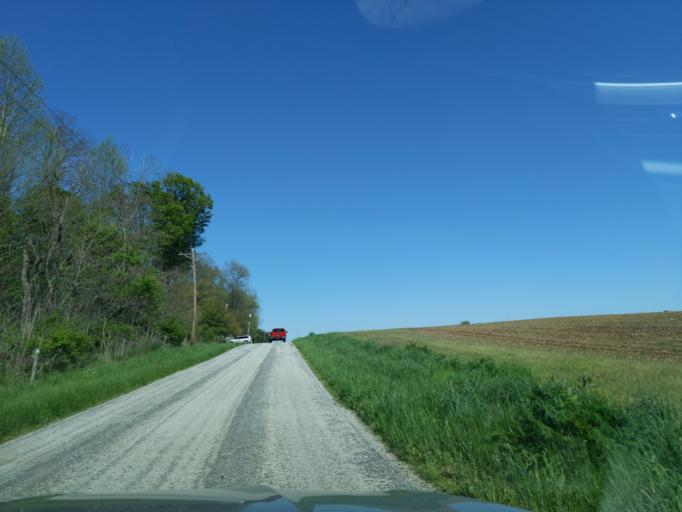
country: US
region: Indiana
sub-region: Decatur County
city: Greensburg
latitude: 39.2928
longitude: -85.4825
